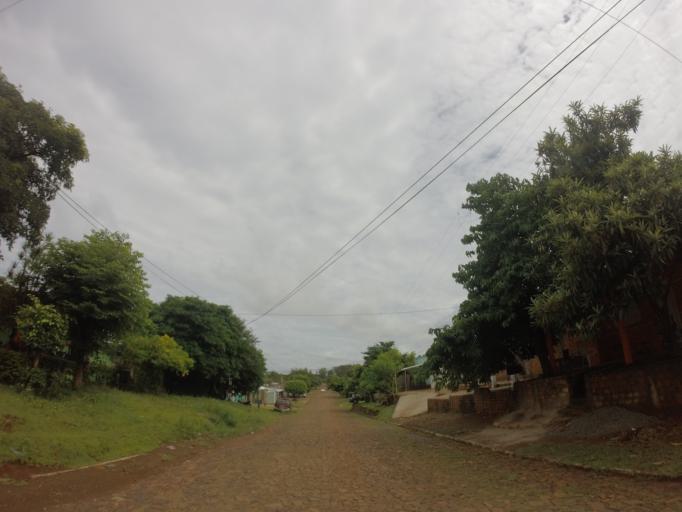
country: PY
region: Alto Parana
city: Ciudad del Este
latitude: -25.3987
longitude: -54.6457
